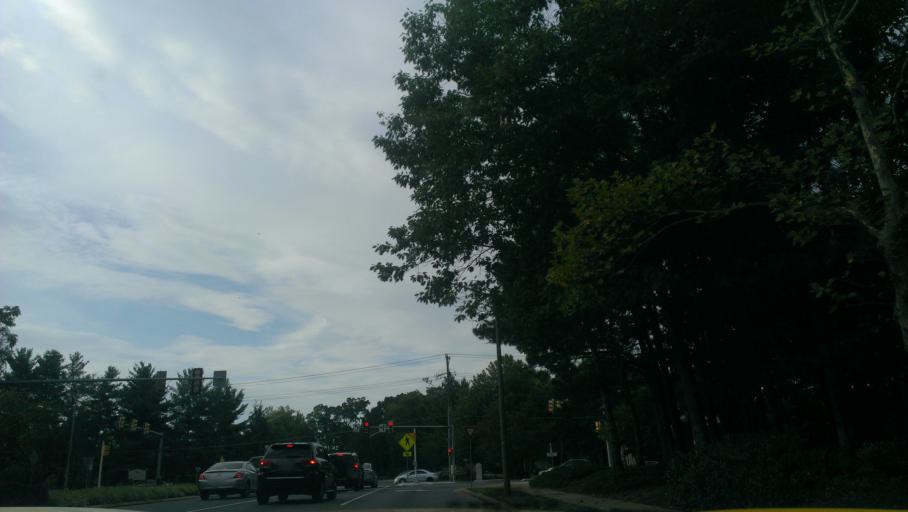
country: US
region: Virginia
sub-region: Fairfax County
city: Merrifield
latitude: 38.8748
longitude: -77.2151
